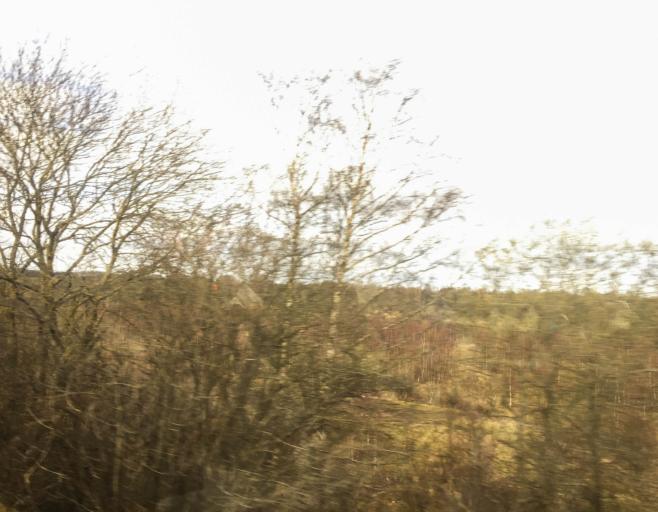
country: GB
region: Scotland
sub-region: North Lanarkshire
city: Newarthill
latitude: 55.7866
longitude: -3.9477
